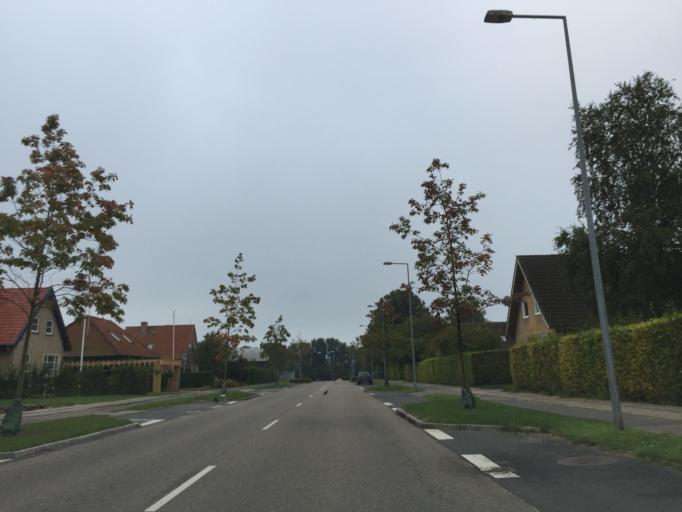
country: DK
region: South Denmark
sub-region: Sonderborg Kommune
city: Sonderborg
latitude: 54.9039
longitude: 9.8013
